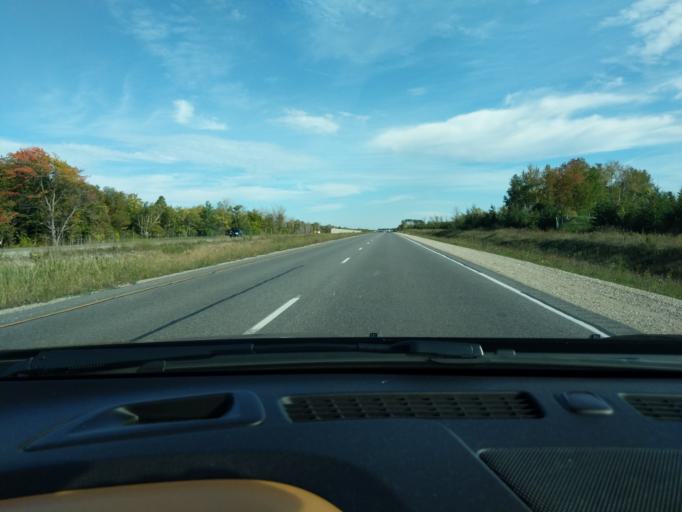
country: CA
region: Ontario
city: Collingwood
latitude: 44.4801
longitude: -80.1654
